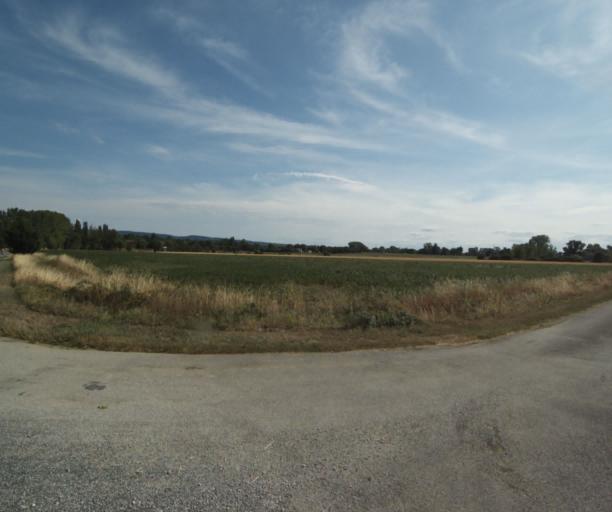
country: FR
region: Midi-Pyrenees
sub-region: Departement de la Haute-Garonne
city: Revel
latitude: 43.4935
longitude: 1.9881
